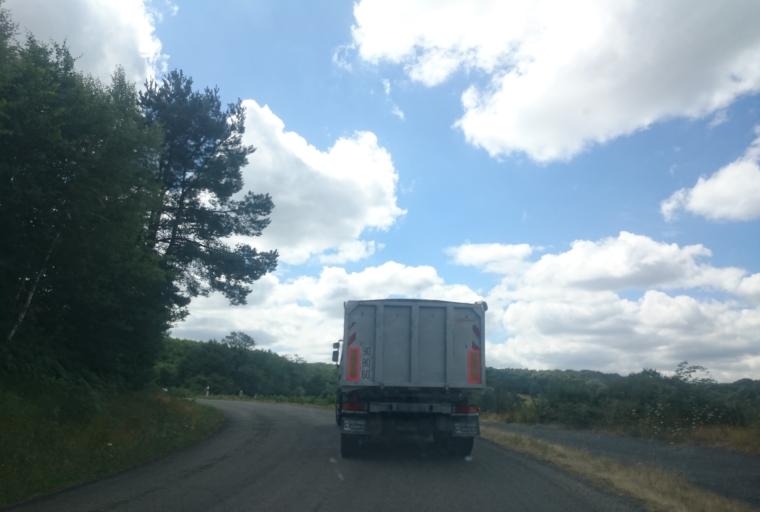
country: FR
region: Auvergne
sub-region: Departement du Cantal
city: Laroquebrou
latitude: 44.9369
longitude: 2.1965
